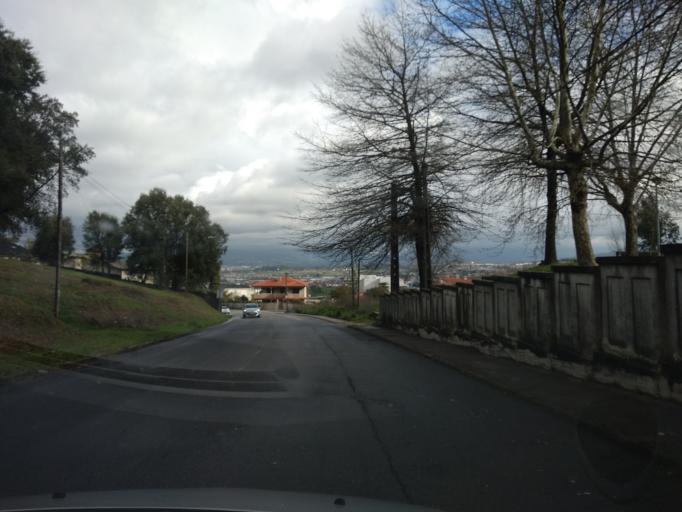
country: PT
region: Braga
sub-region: Braga
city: Braga
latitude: 41.5430
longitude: -8.4426
